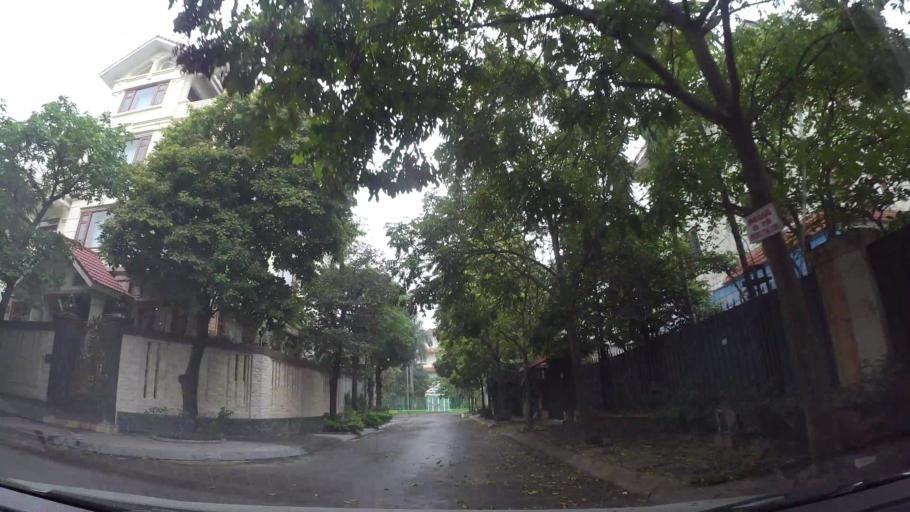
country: VN
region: Ha Noi
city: Cau Giay
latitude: 21.0205
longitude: 105.7974
